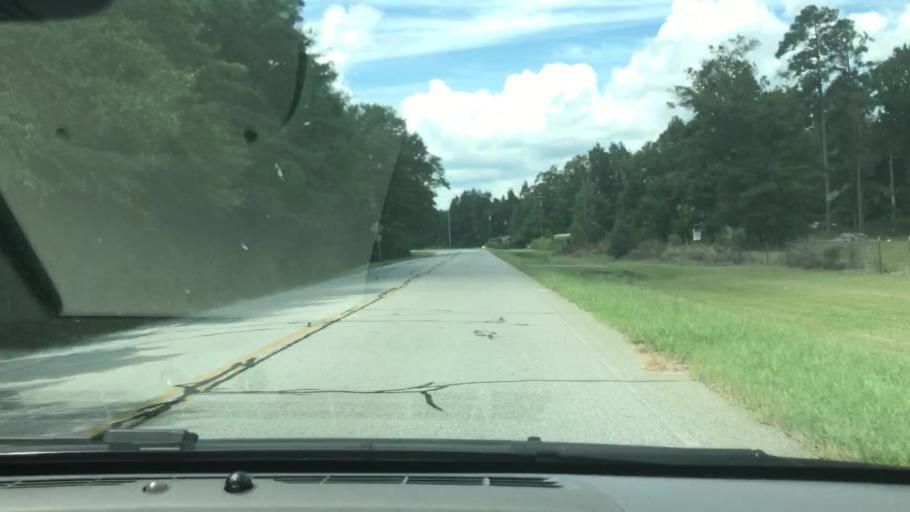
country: US
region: Georgia
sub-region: Stewart County
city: Lumpkin
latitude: 32.1433
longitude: -85.0148
